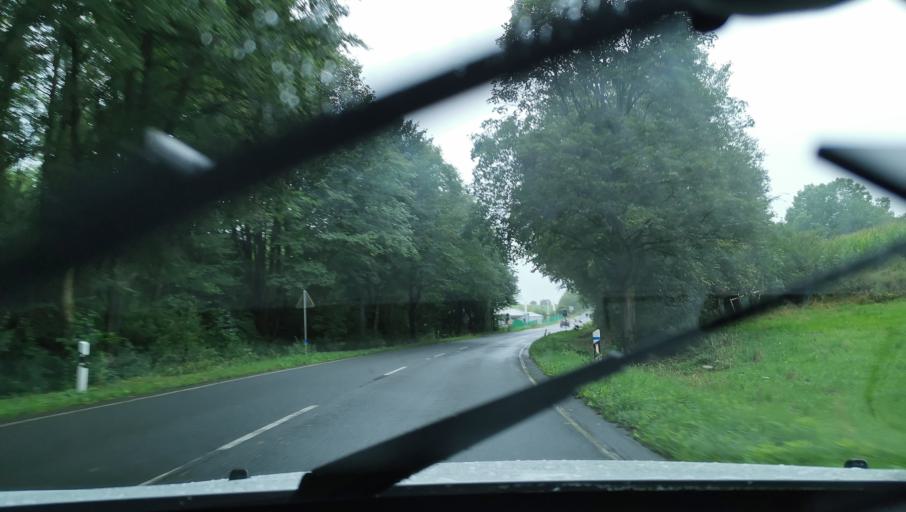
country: DE
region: North Rhine-Westphalia
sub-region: Regierungsbezirk Arnsberg
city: Breckerfeld
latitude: 51.2467
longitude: 7.4837
